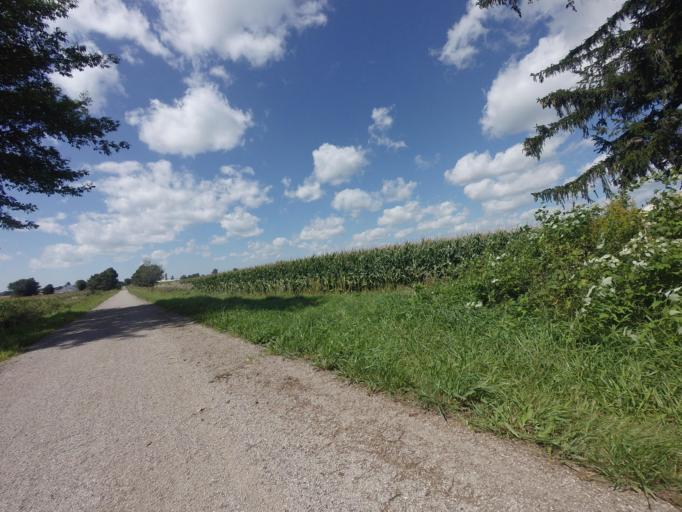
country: CA
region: Ontario
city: Huron East
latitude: 43.6613
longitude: -81.2536
